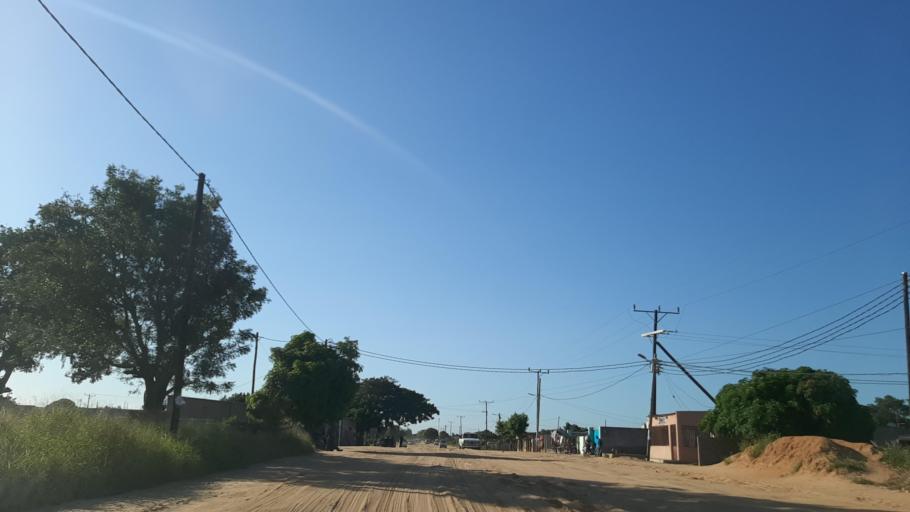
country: MZ
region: Maputo City
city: Maputo
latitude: -25.7506
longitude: 32.5470
